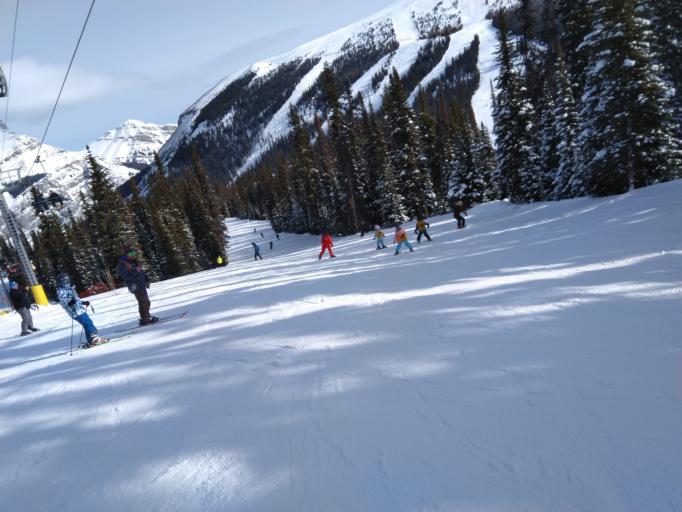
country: CA
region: Alberta
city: Banff
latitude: 51.0846
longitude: -115.7726
